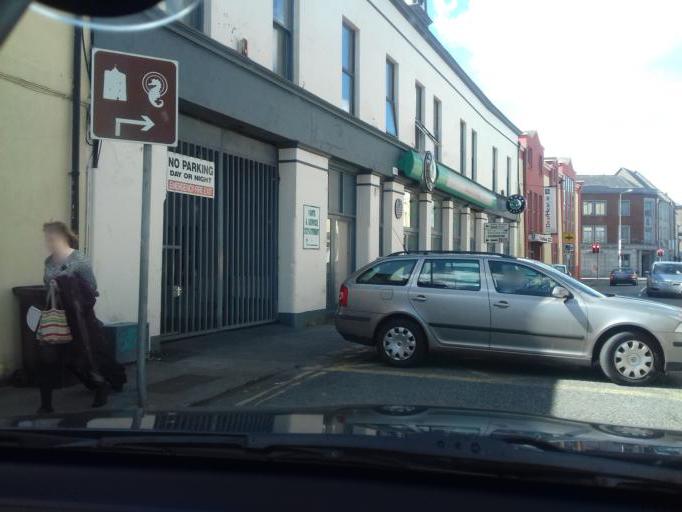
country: IE
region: Munster
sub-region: Waterford
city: Waterford
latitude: 52.2584
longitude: -7.1078
